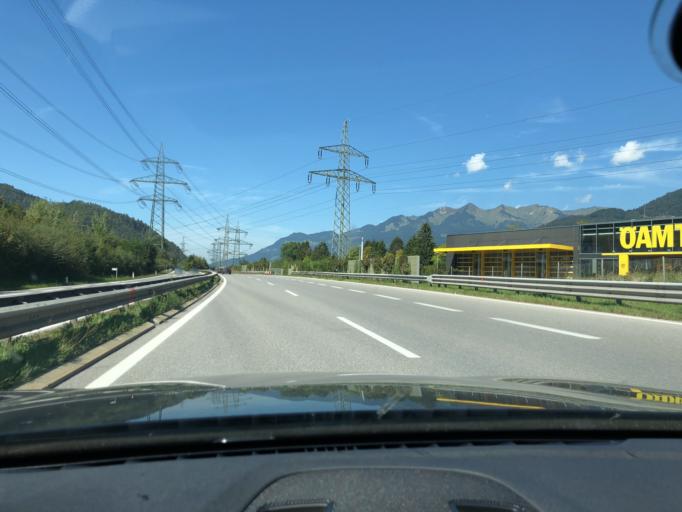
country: AT
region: Vorarlberg
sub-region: Politischer Bezirk Bludenz
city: Bludenz
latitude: 47.1526
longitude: 9.8125
